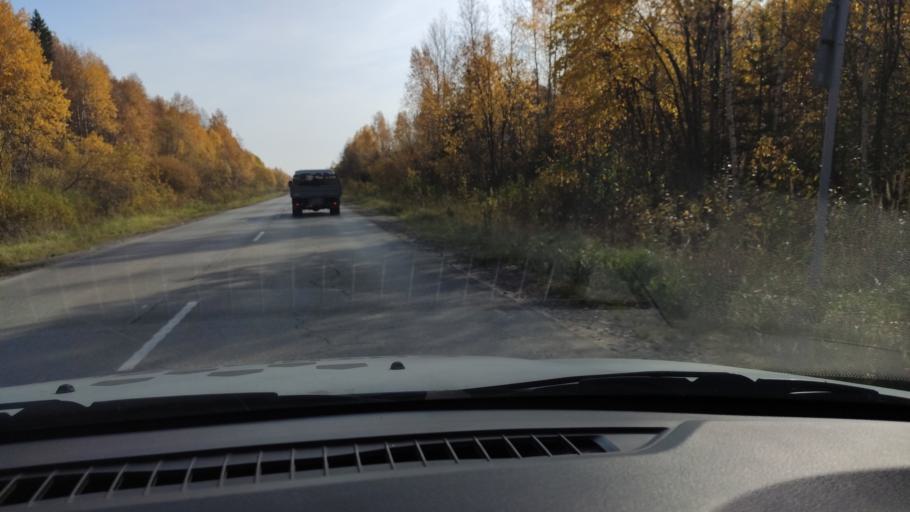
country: RU
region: Perm
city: Novyye Lyady
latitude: 58.0300
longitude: 56.6205
